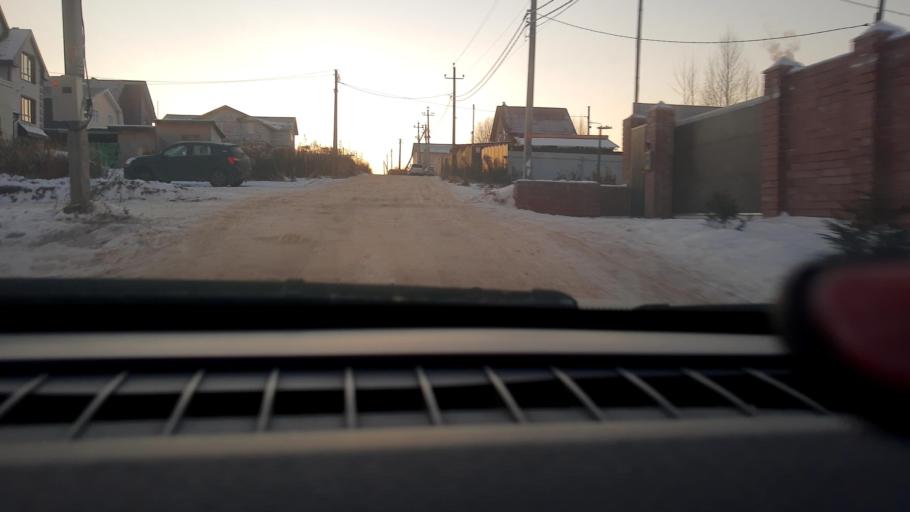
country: RU
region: Nizjnij Novgorod
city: Afonino
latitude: 56.2706
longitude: 44.0581
